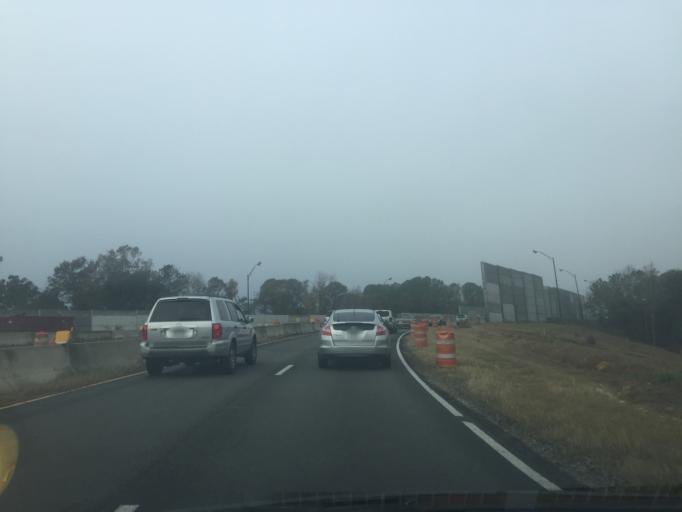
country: US
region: Georgia
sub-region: Chatham County
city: Georgetown
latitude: 31.9878
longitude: -81.2206
